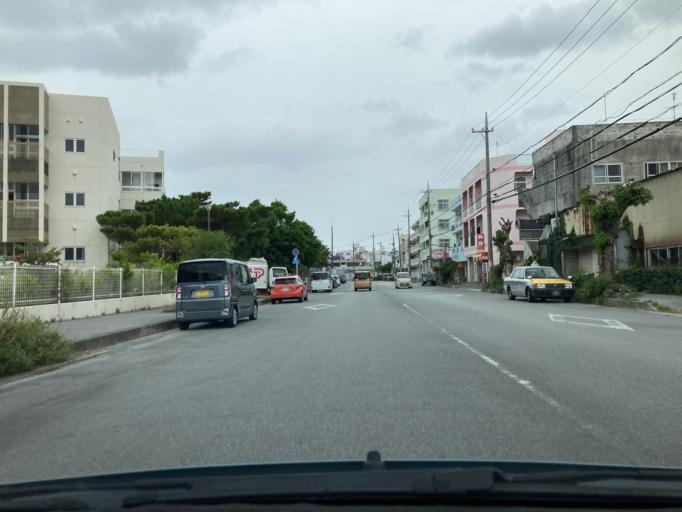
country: JP
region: Okinawa
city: Itoman
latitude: 26.1357
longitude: 127.6671
